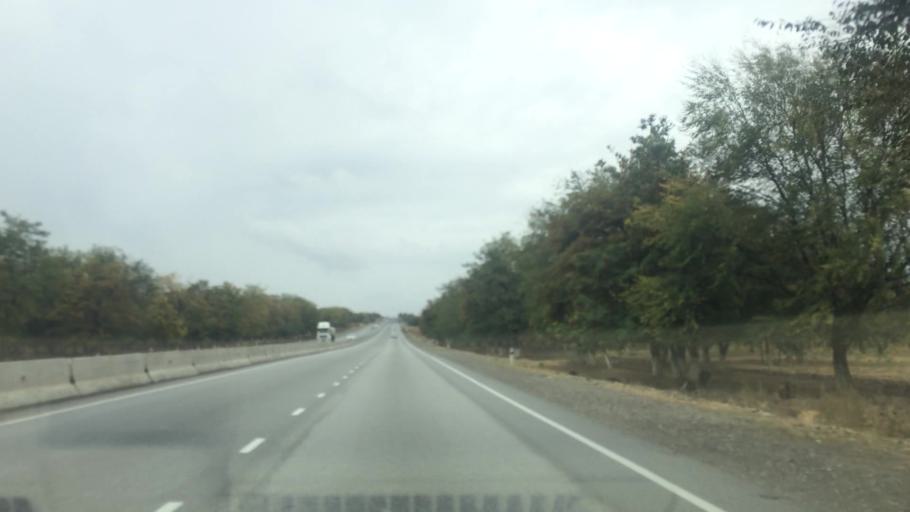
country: UZ
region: Samarqand
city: Bulung'ur
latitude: 39.8699
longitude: 67.4772
